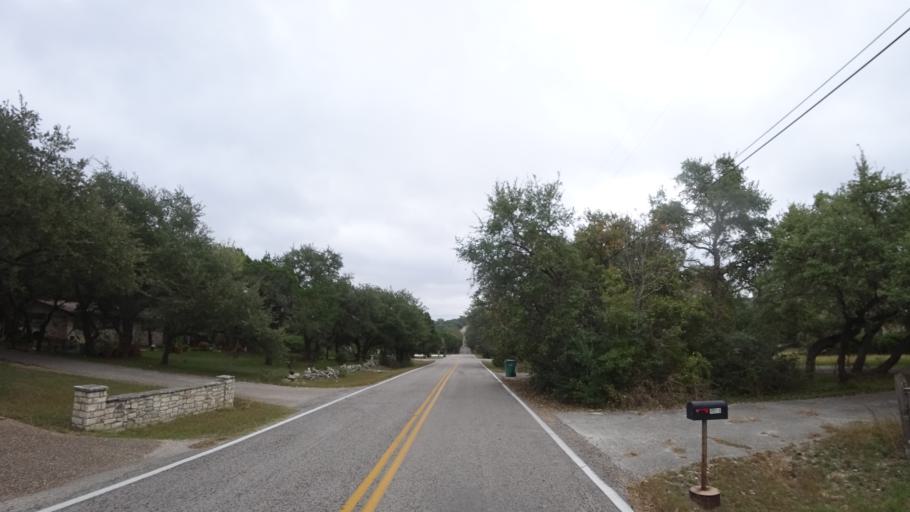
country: US
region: Texas
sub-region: Travis County
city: Barton Creek
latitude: 30.2622
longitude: -97.9163
